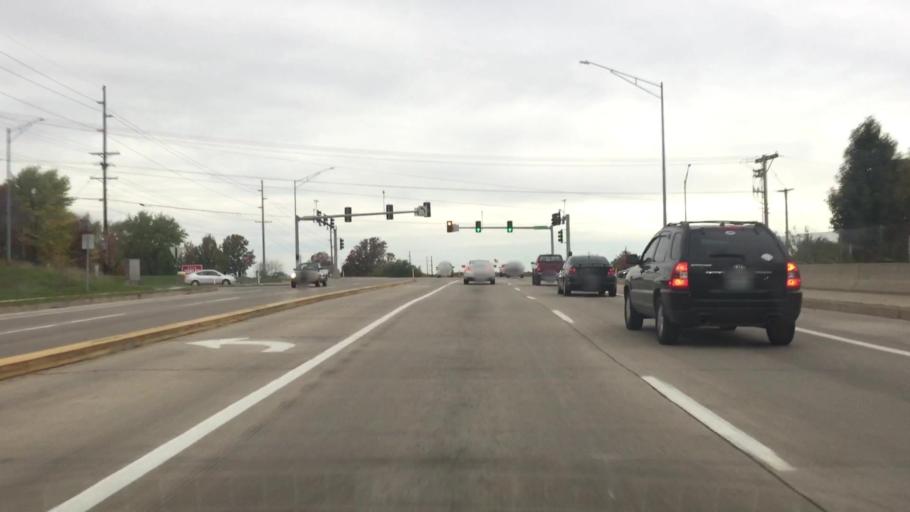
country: US
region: Missouri
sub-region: Boone County
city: Columbia
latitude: 38.9134
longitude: -92.3124
